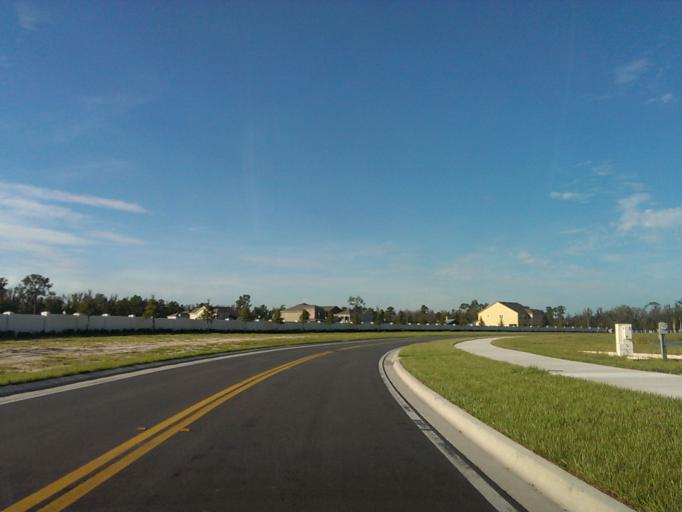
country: US
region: Florida
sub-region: Orange County
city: Lake Butler
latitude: 28.4327
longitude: -81.6053
